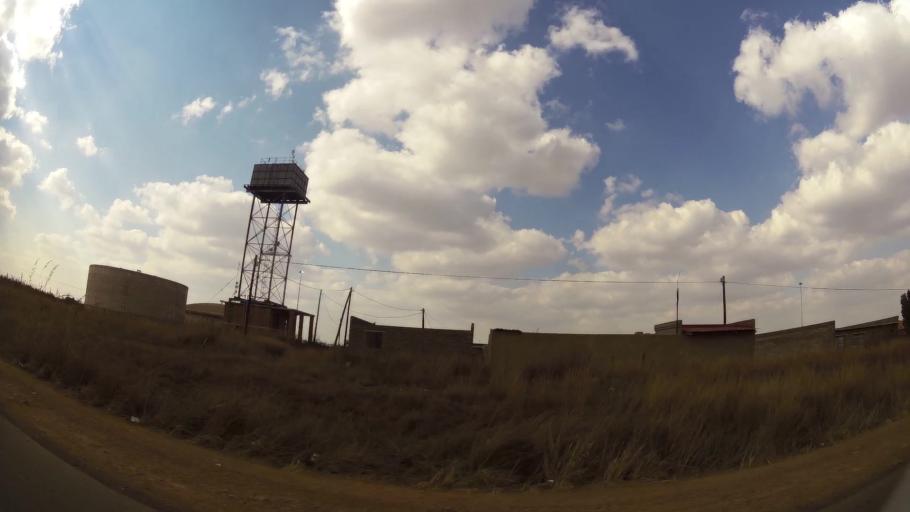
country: ZA
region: Mpumalanga
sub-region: Nkangala District Municipality
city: Delmas
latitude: -26.0989
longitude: 28.6779
